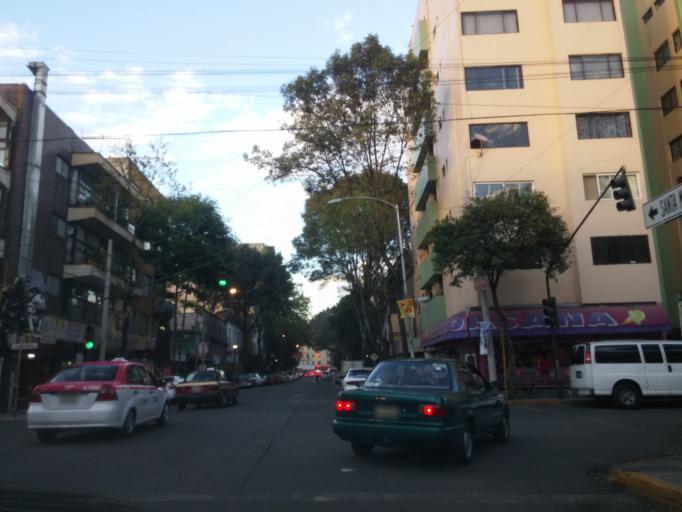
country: MX
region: Mexico City
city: Cuauhtemoc
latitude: 19.4391
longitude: -99.1591
